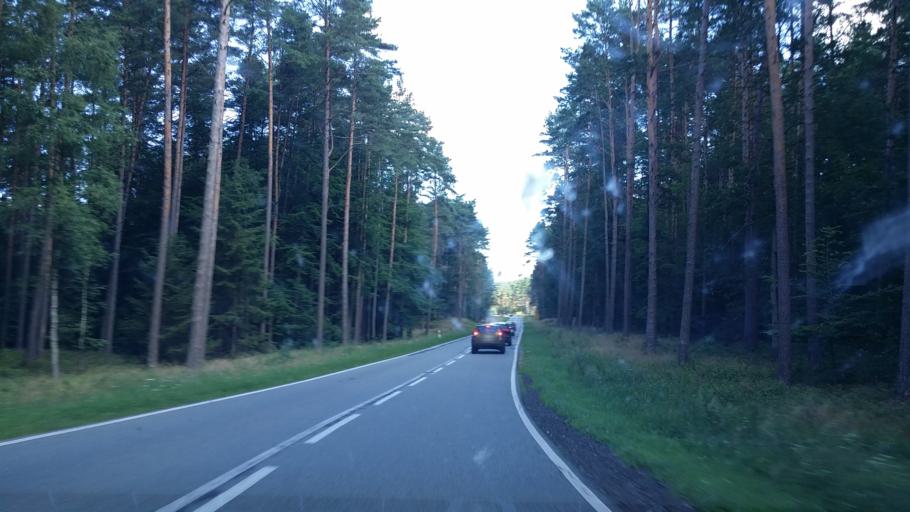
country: PL
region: West Pomeranian Voivodeship
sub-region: Powiat drawski
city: Drawsko Pomorskie
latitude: 53.4269
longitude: 15.8271
